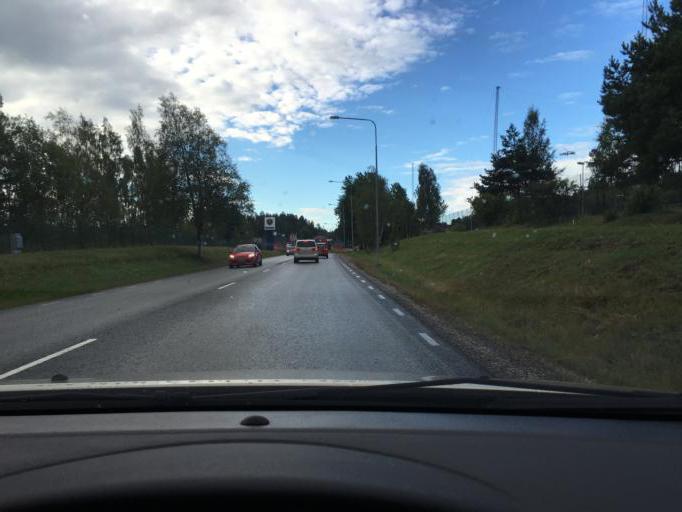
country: SE
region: Stockholm
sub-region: Sodertalje Kommun
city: Pershagen
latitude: 59.1675
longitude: 17.6392
